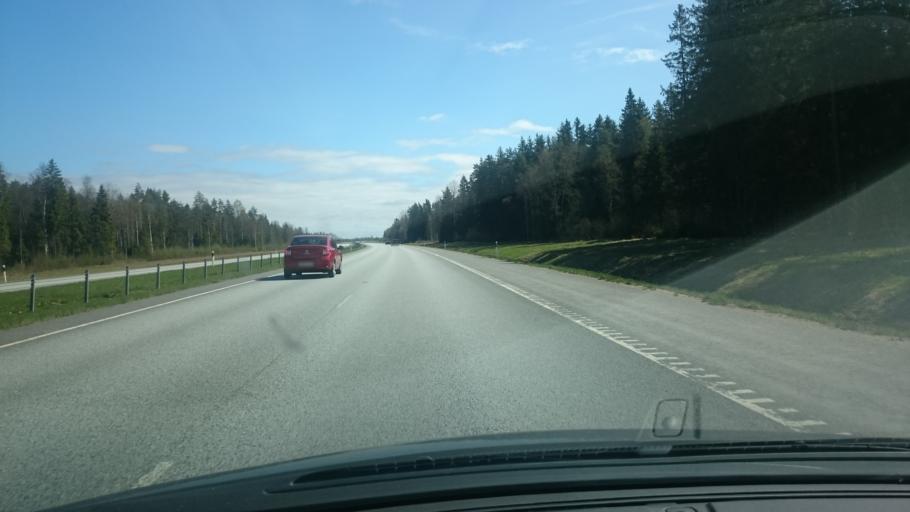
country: EE
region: Laeaene-Virumaa
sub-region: Tapa vald
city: Tapa
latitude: 59.4575
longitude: 25.9723
